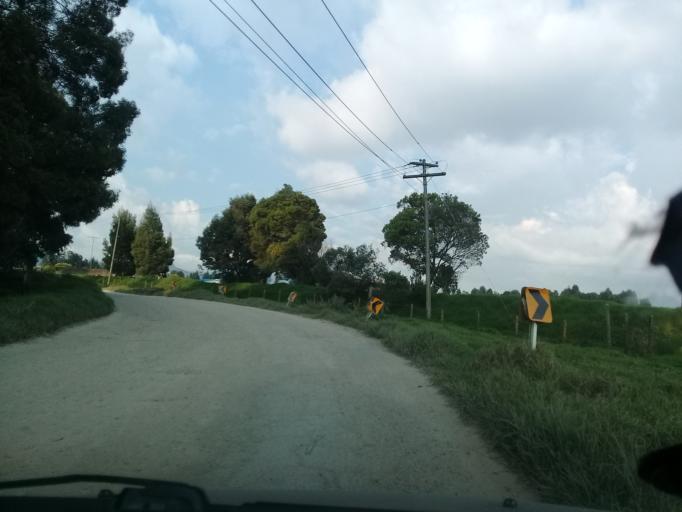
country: CO
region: Cundinamarca
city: Funza
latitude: 4.7634
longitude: -74.2210
